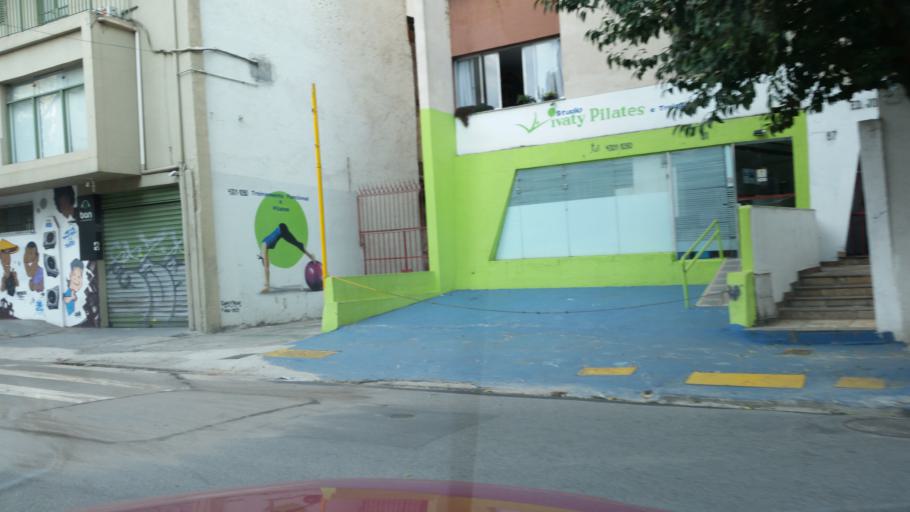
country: BR
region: Sao Paulo
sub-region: Sao Paulo
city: Sao Paulo
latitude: -23.5665
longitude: -46.6453
